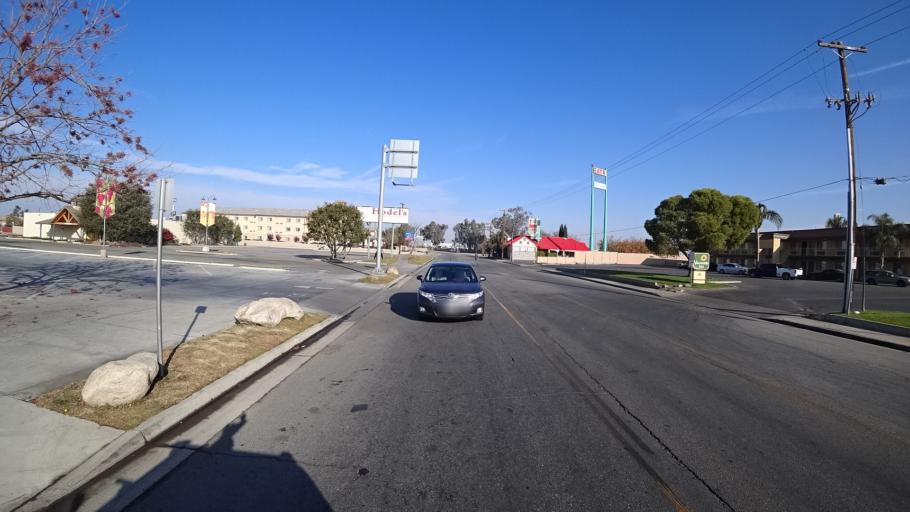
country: US
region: California
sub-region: Kern County
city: Oildale
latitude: 35.4136
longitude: -119.0588
